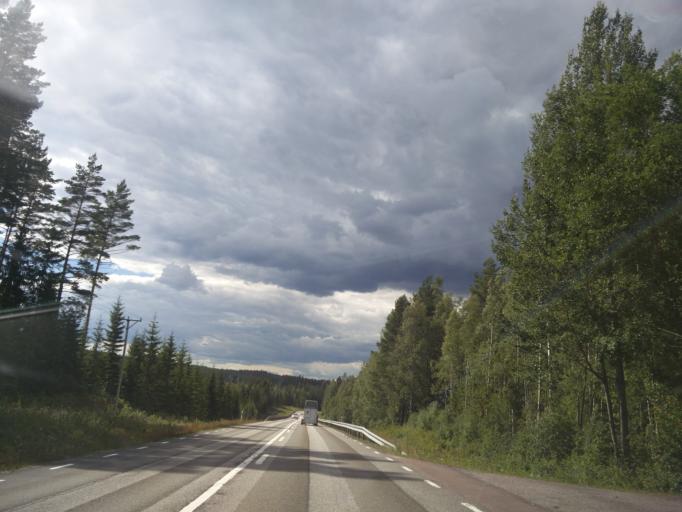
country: SE
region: OErebro
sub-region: Hallefors Kommun
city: Haellefors
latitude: 59.7648
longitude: 14.4173
